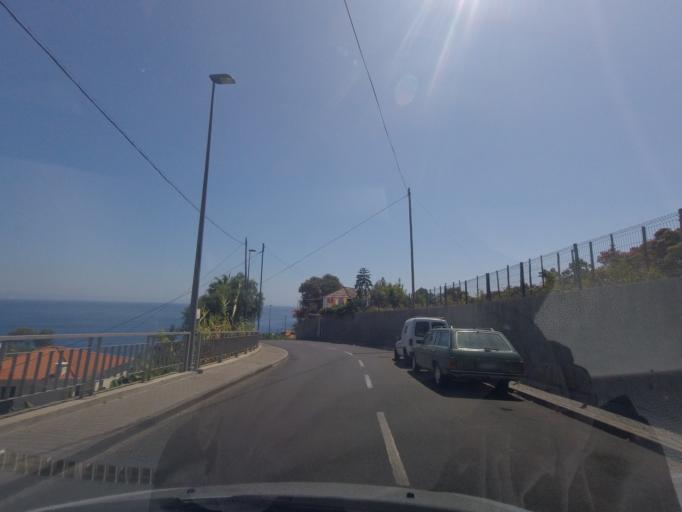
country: PT
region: Madeira
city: Camara de Lobos
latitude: 32.6480
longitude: -16.9616
